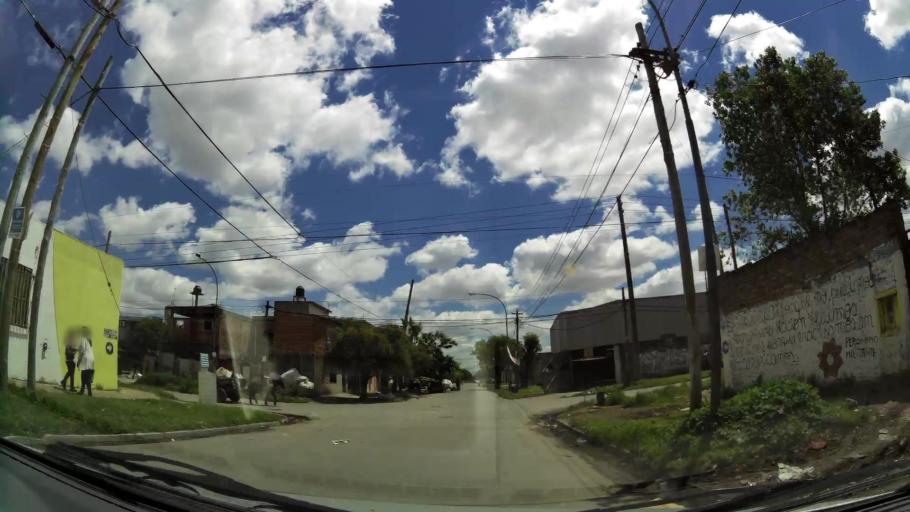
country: AR
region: Buenos Aires
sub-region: Partido de Lanus
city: Lanus
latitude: -34.7038
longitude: -58.4338
